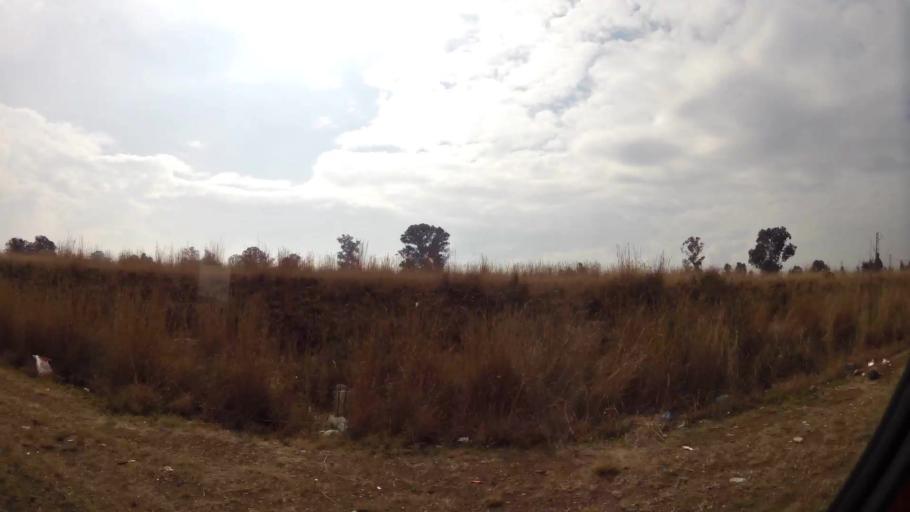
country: ZA
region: Gauteng
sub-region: Sedibeng District Municipality
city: Vanderbijlpark
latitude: -26.6861
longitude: 27.8556
